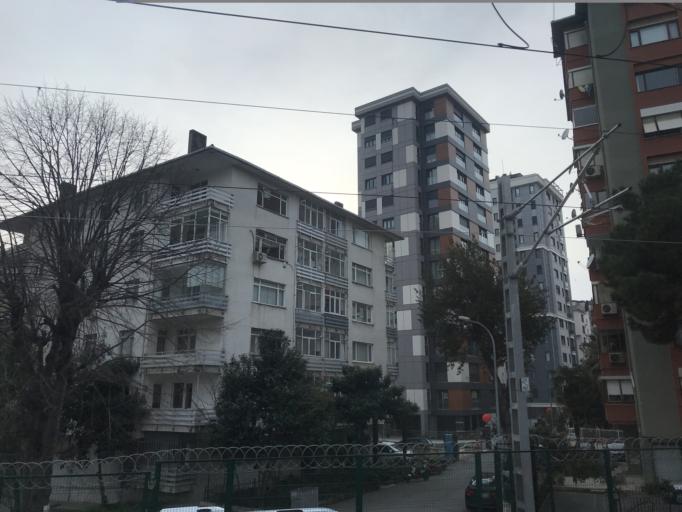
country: TR
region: Istanbul
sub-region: Atasehir
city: Atasehir
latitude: 40.9687
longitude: 29.0776
